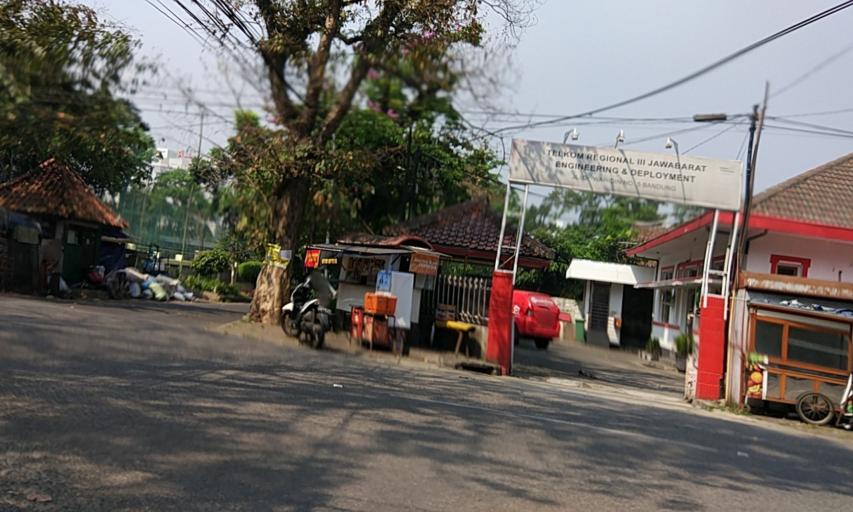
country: ID
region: West Java
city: Bandung
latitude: -6.9039
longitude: 107.5985
